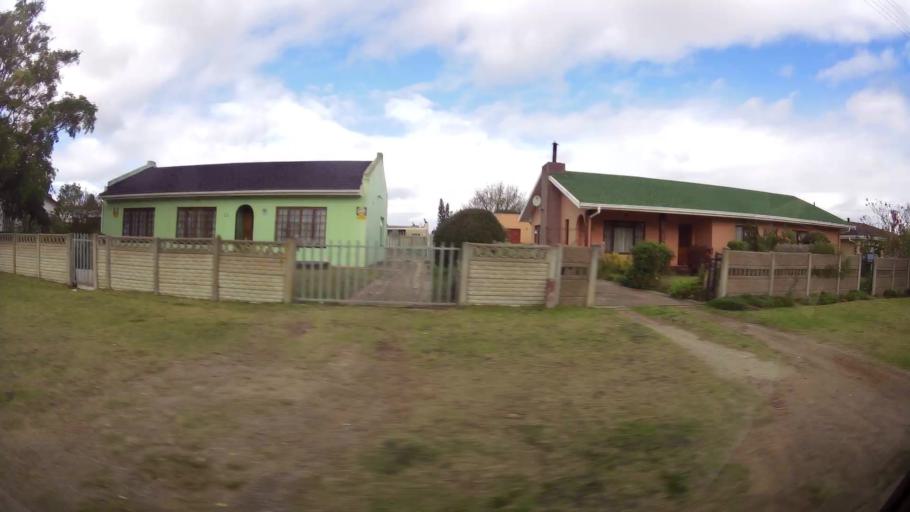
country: ZA
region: Western Cape
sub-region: Eden District Municipality
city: George
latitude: -34.0072
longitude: 22.4416
